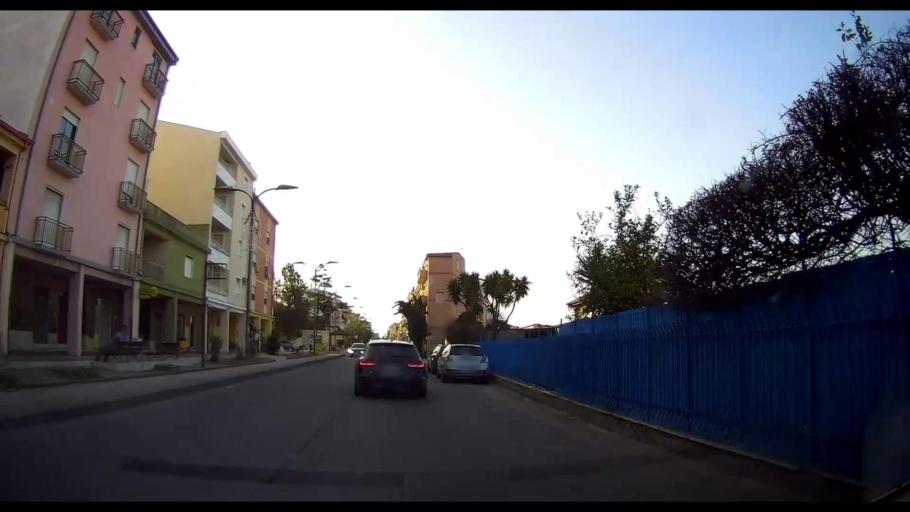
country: IT
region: Calabria
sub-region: Provincia di Crotone
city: Torretta
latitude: 39.4496
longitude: 17.0402
